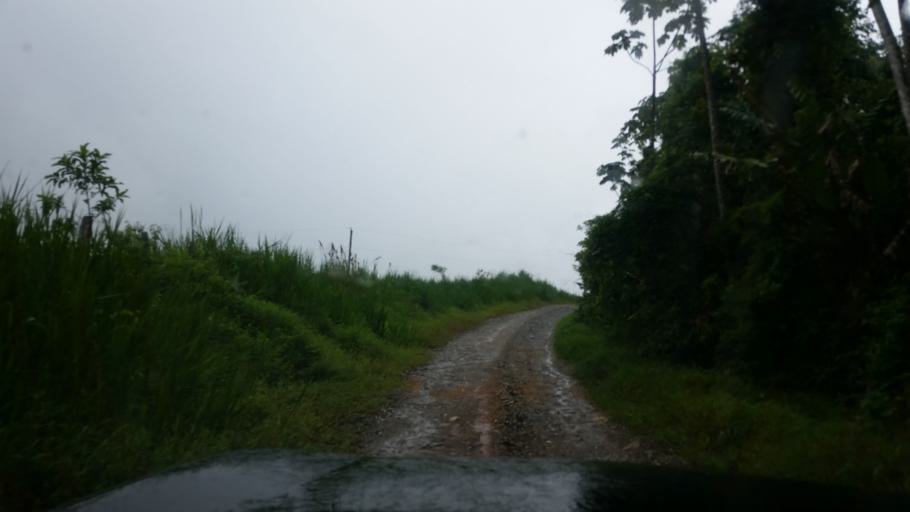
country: NI
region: Atlantico Norte (RAAN)
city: Bonanza
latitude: 14.0790
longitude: -84.6661
